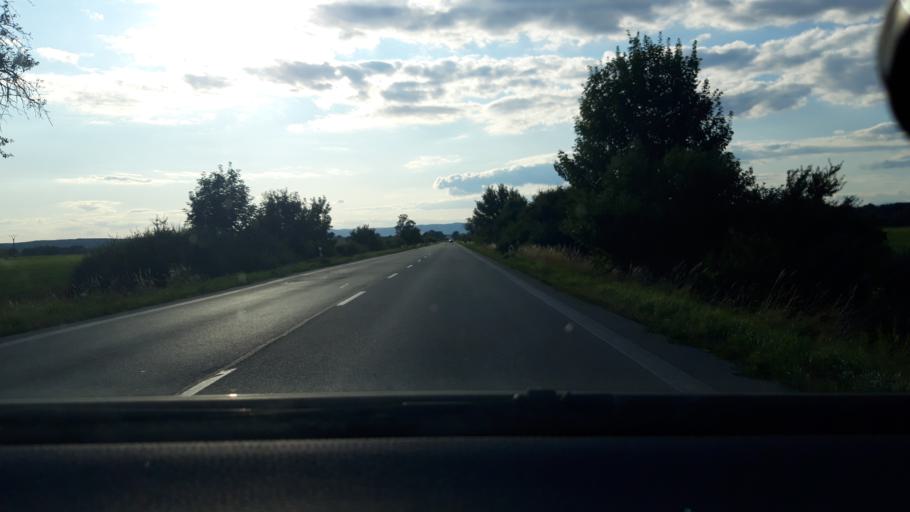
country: SK
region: Banskobystricky
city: Lucenec
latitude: 48.3006
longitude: 19.7361
